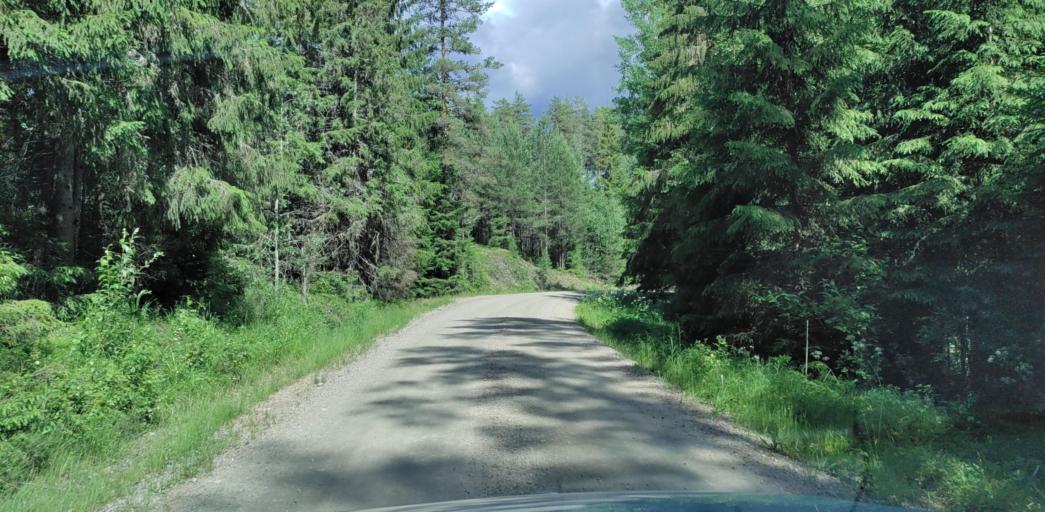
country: SE
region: Vaermland
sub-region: Sunne Kommun
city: Sunne
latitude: 60.0536
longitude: 13.2678
